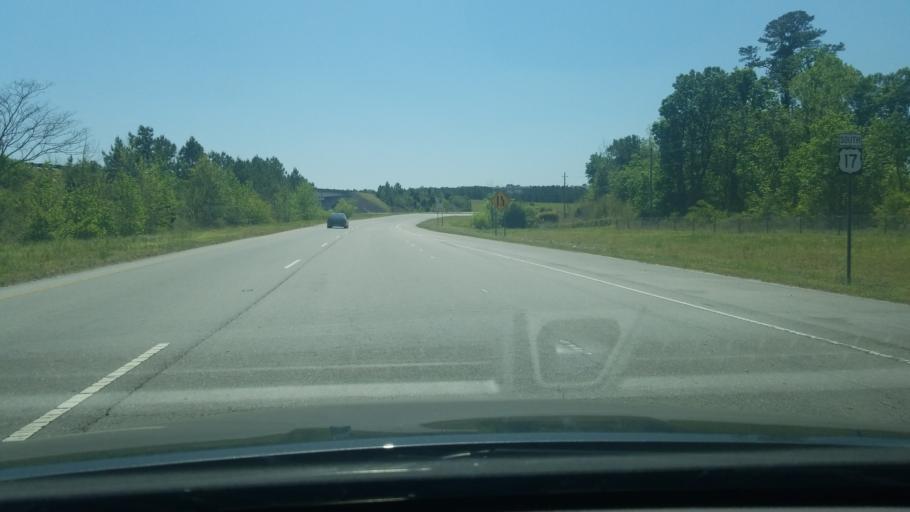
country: US
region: North Carolina
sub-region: Onslow County
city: Jacksonville
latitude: 34.7429
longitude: -77.4585
